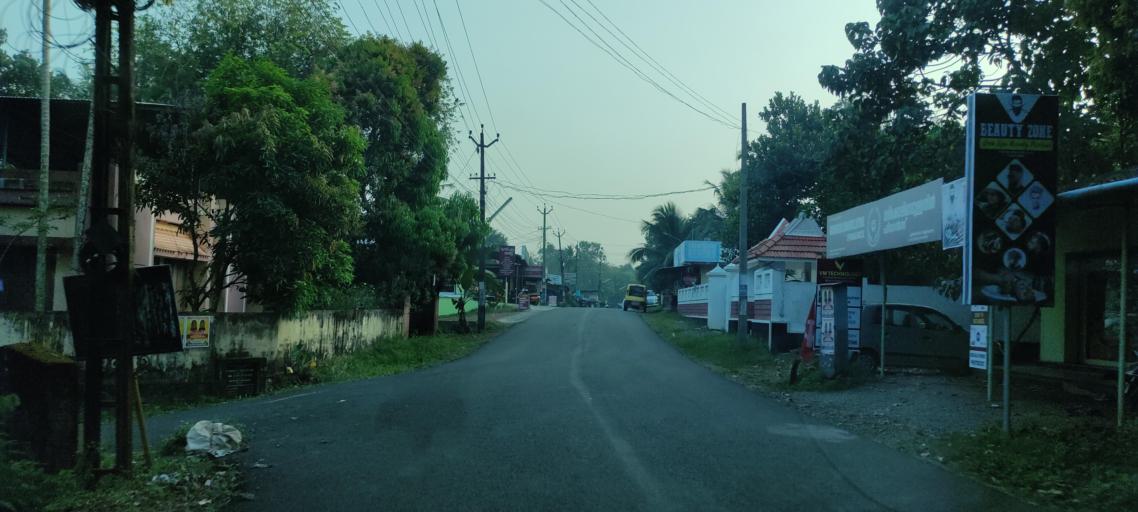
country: IN
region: Kerala
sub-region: Alappuzha
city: Kattanam
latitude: 9.1475
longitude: 76.5753
